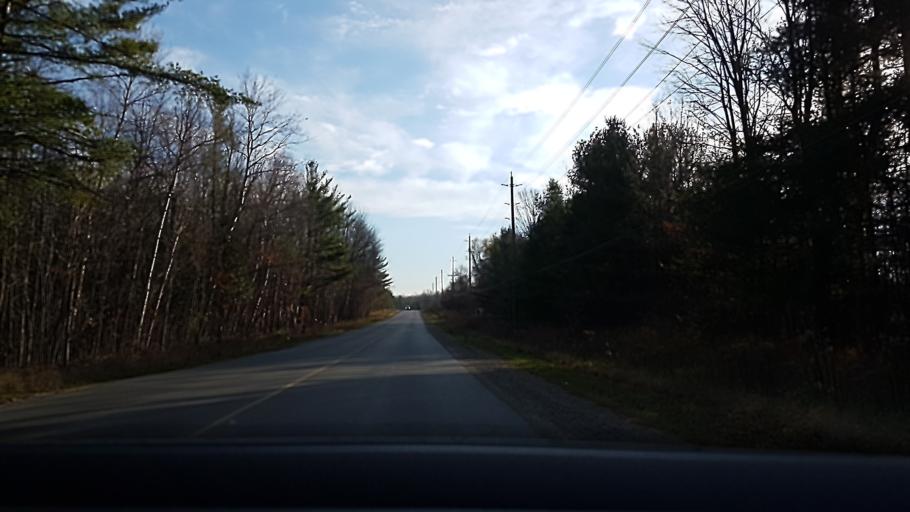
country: CA
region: Ontario
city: Barrie
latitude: 44.3713
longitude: -79.5520
